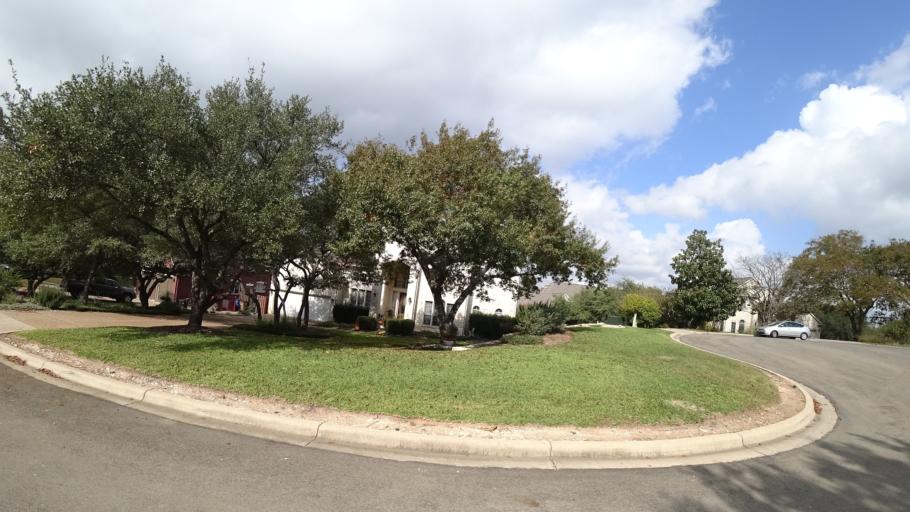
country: US
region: Texas
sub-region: Williamson County
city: Anderson Mill
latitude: 30.4218
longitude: -97.8554
